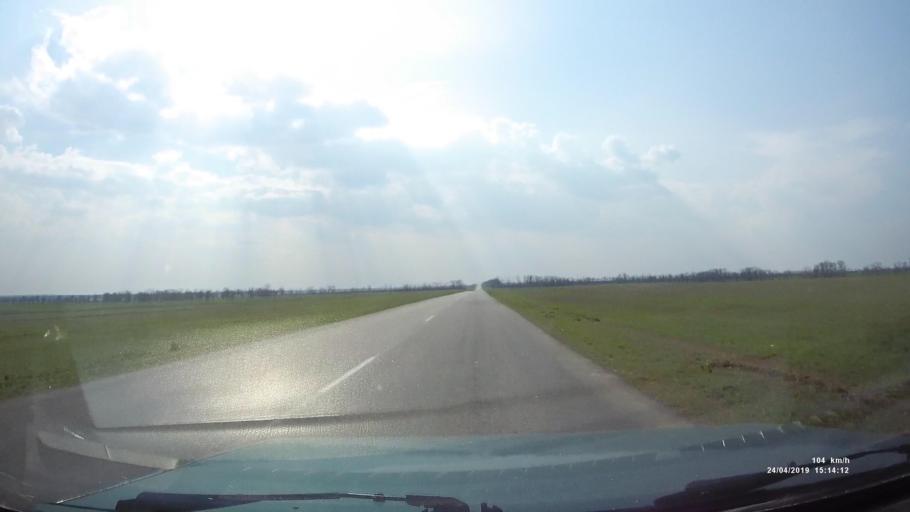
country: RU
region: Rostov
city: Remontnoye
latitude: 46.5463
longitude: 43.2629
